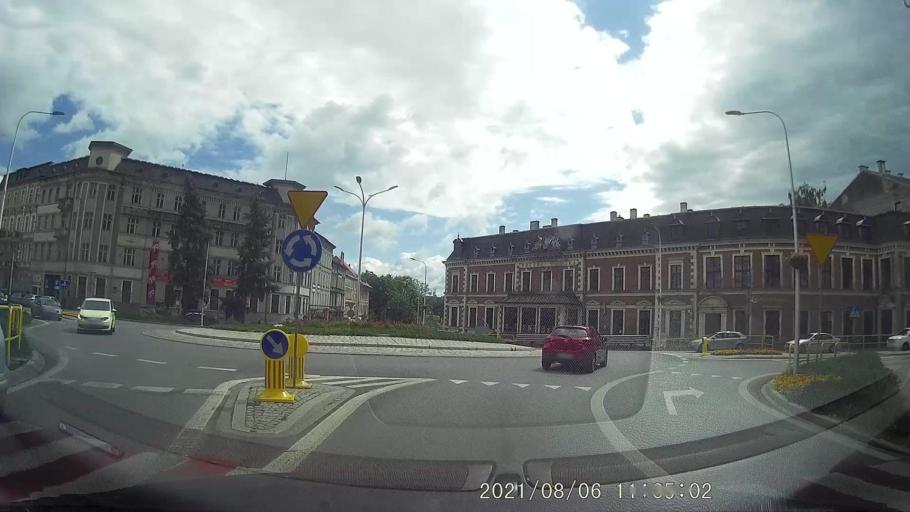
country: PL
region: Lower Silesian Voivodeship
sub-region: Powiat klodzki
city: Klodzko
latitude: 50.4360
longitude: 16.6497
